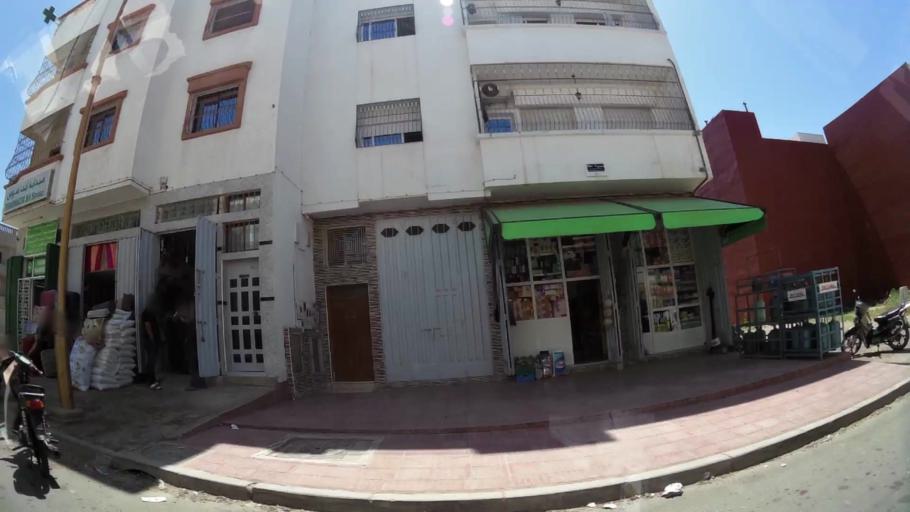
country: MA
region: Oued ed Dahab-Lagouira
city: Dakhla
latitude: 30.4290
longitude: -9.5538
